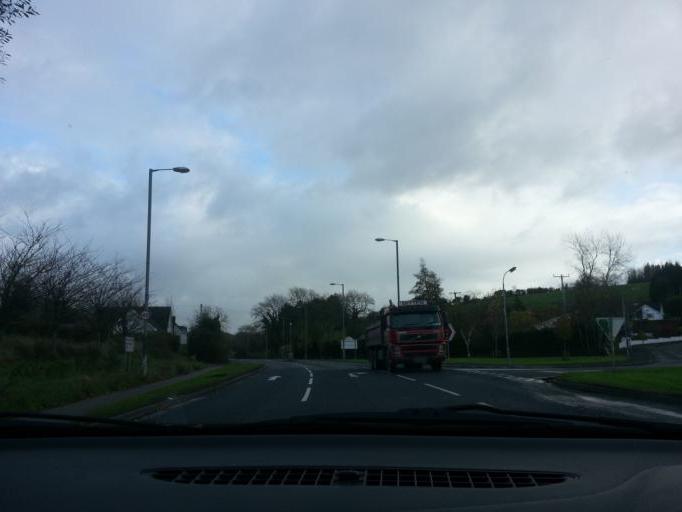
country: GB
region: Northern Ireland
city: Lisnaskea
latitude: 54.2445
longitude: -7.4355
